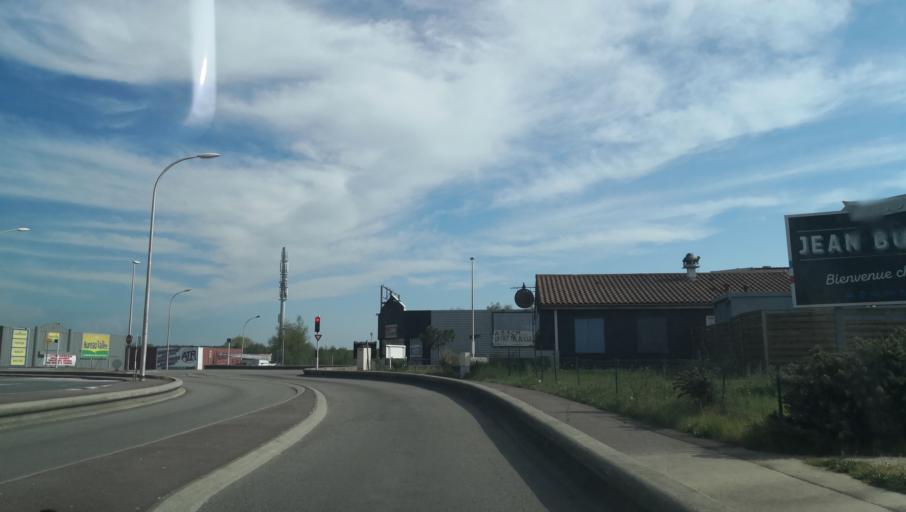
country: FR
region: Limousin
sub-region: Departement de la Haute-Vienne
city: Couzeix
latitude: 45.8686
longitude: 1.2637
